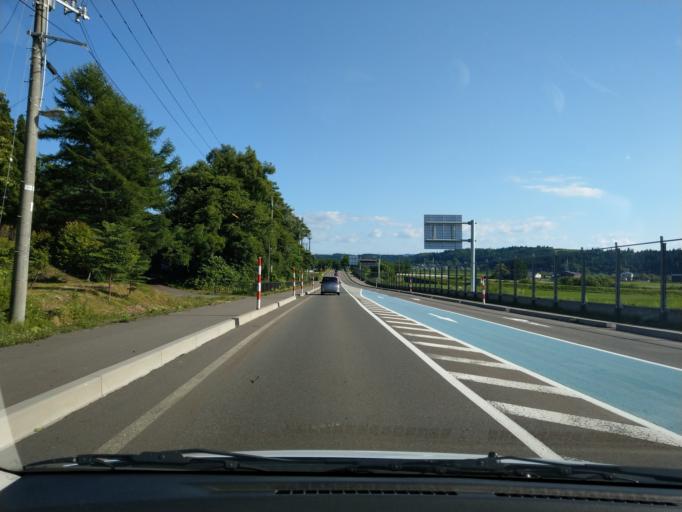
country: JP
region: Akita
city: Takanosu
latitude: 40.2014
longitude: 140.3962
